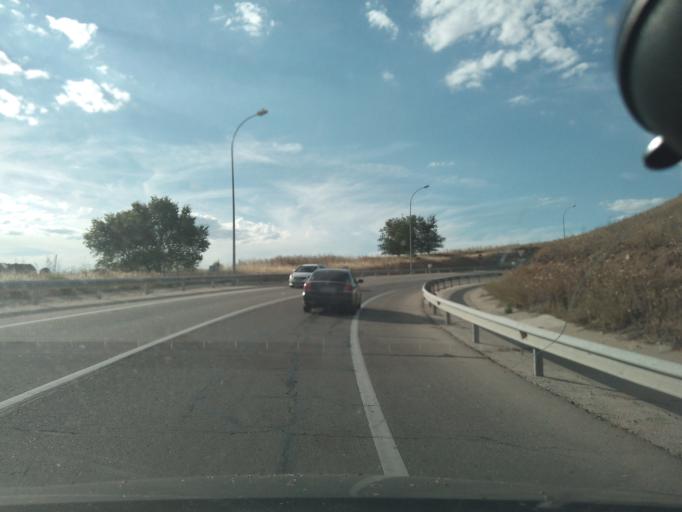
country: ES
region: Madrid
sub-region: Provincia de Madrid
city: Torrejon de Ardoz
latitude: 40.4805
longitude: -3.4971
